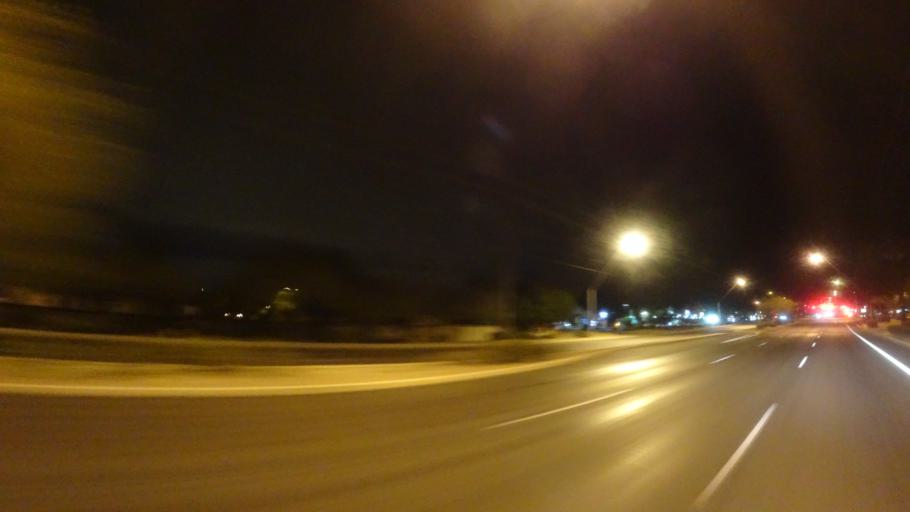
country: US
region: Arizona
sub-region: Maricopa County
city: Gilbert
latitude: 33.4348
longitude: -111.6842
